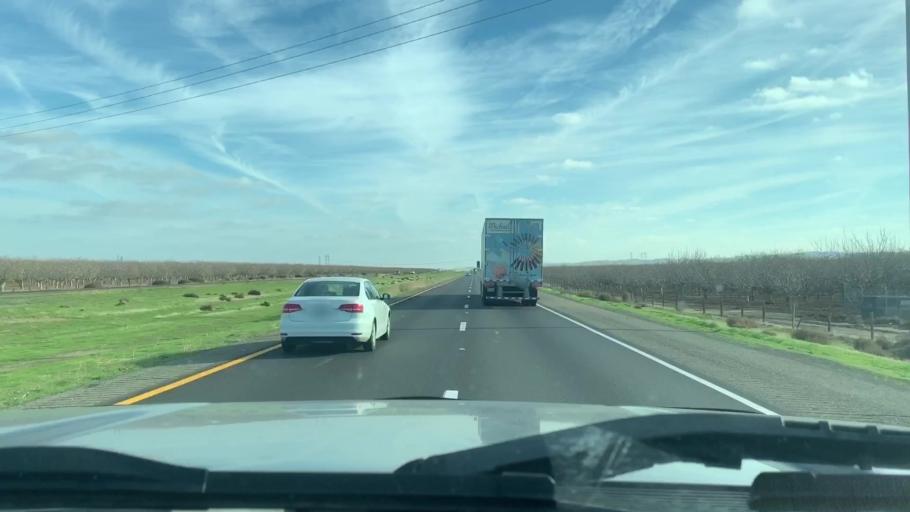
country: US
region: California
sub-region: Fresno County
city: Huron
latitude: 36.1234
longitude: -120.1459
